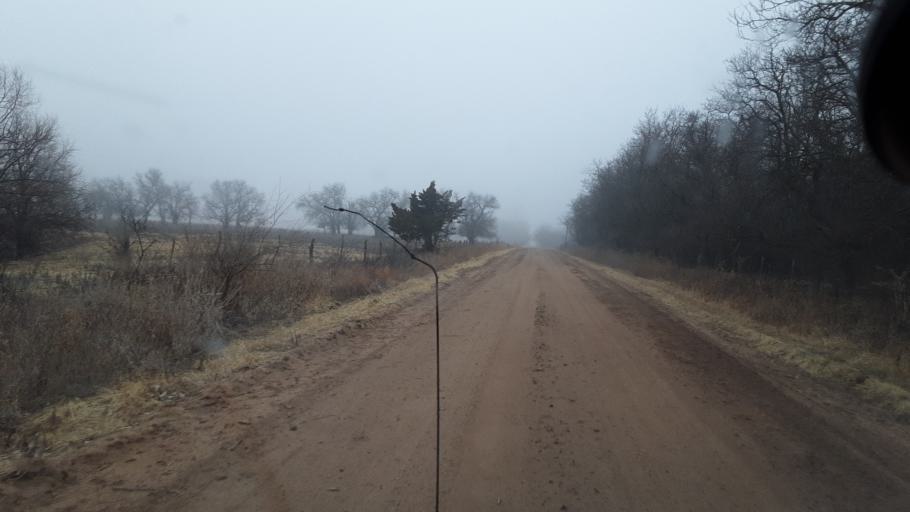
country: US
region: Kansas
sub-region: Reno County
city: South Hutchinson
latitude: 37.9066
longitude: -97.9954
